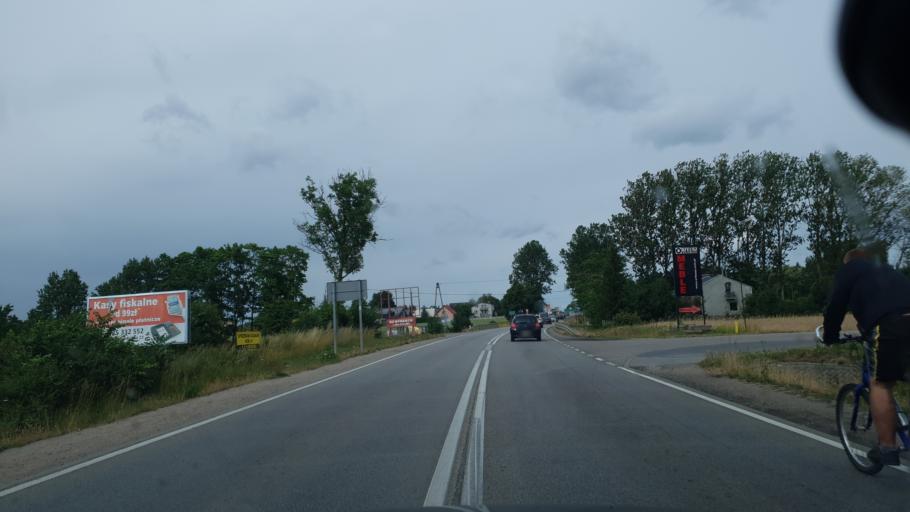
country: PL
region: Pomeranian Voivodeship
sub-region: Powiat kartuski
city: Banino
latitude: 54.4149
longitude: 18.3742
